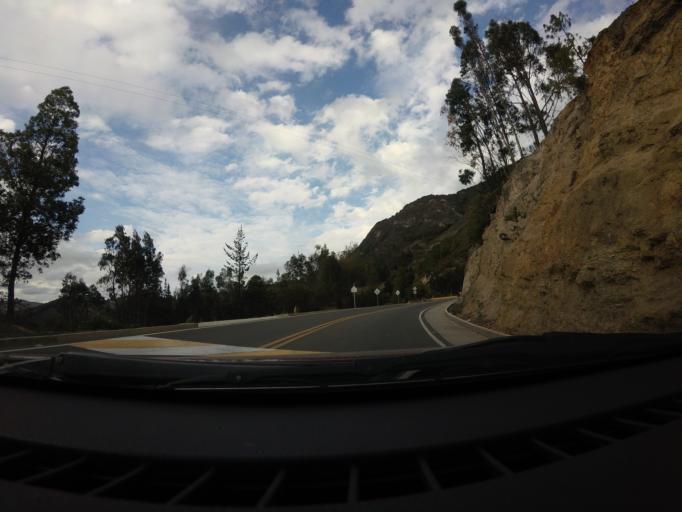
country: CO
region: Boyaca
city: Cucaita
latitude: 5.5510
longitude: -73.4344
